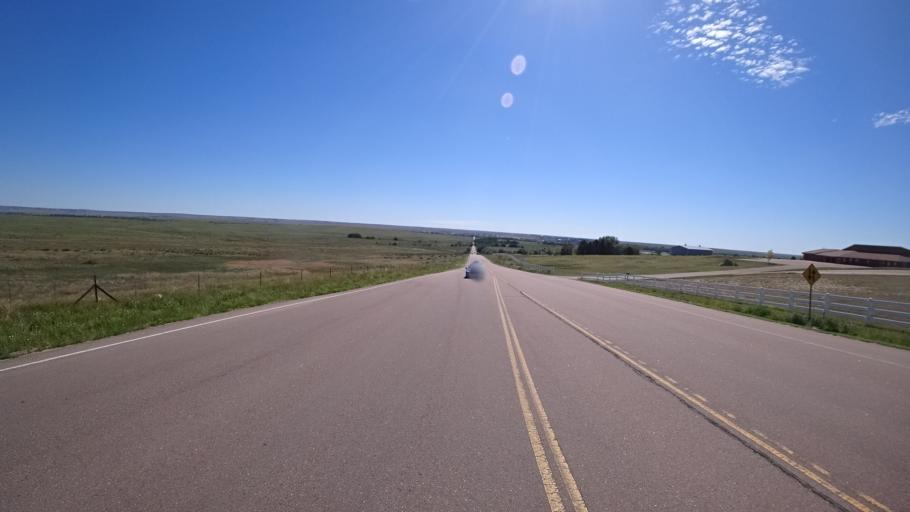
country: US
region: Colorado
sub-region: El Paso County
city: Security-Widefield
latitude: 38.7374
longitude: -104.6811
